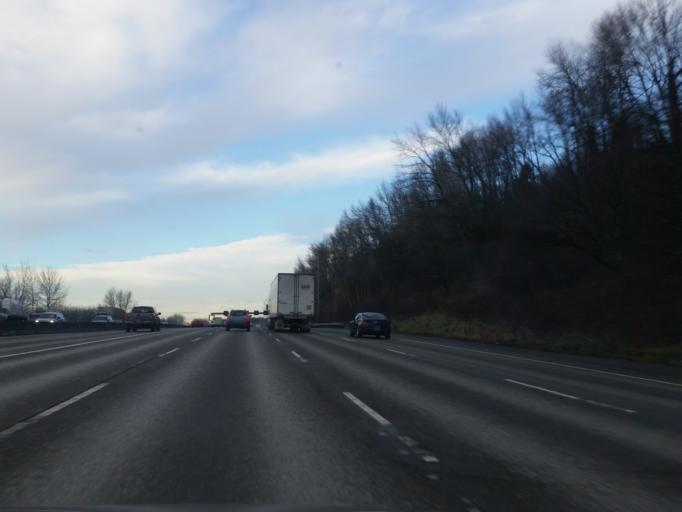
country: US
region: Washington
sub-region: King County
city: Riverton
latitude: 47.5175
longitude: -122.2885
